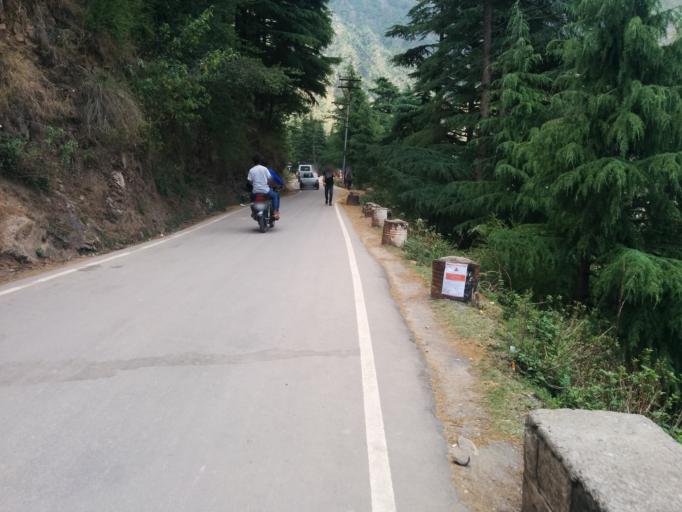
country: IN
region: Himachal Pradesh
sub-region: Kangra
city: Dharmsala
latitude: 32.2399
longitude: 76.3319
